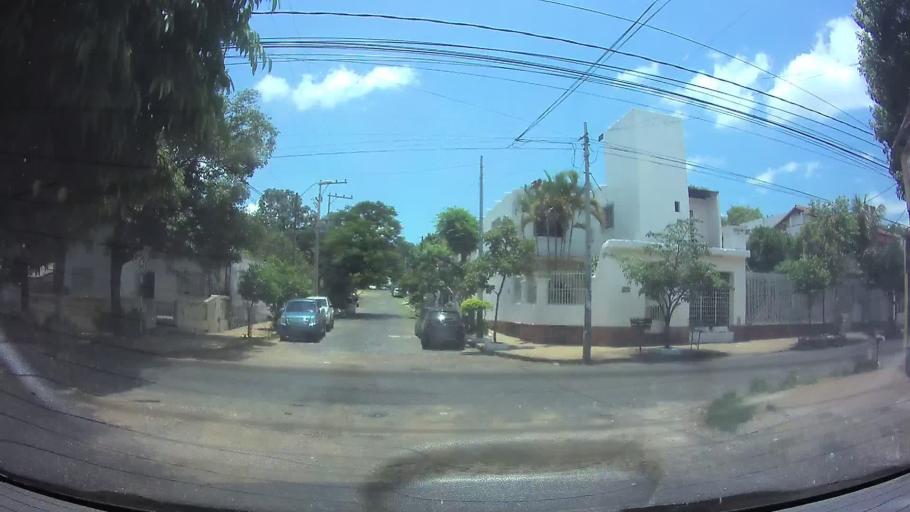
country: PY
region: Asuncion
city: Asuncion
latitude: -25.2998
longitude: -57.6153
